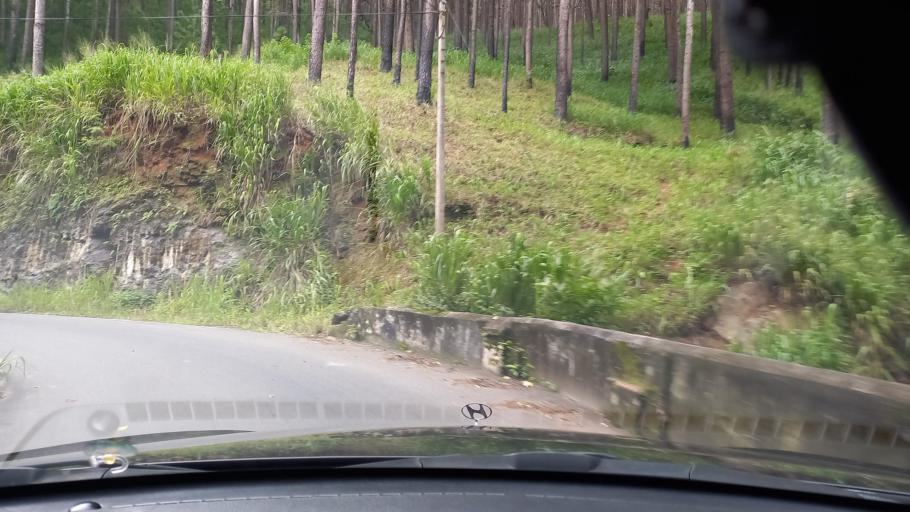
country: LK
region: Central
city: Gampola
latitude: 7.2137
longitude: 80.6206
